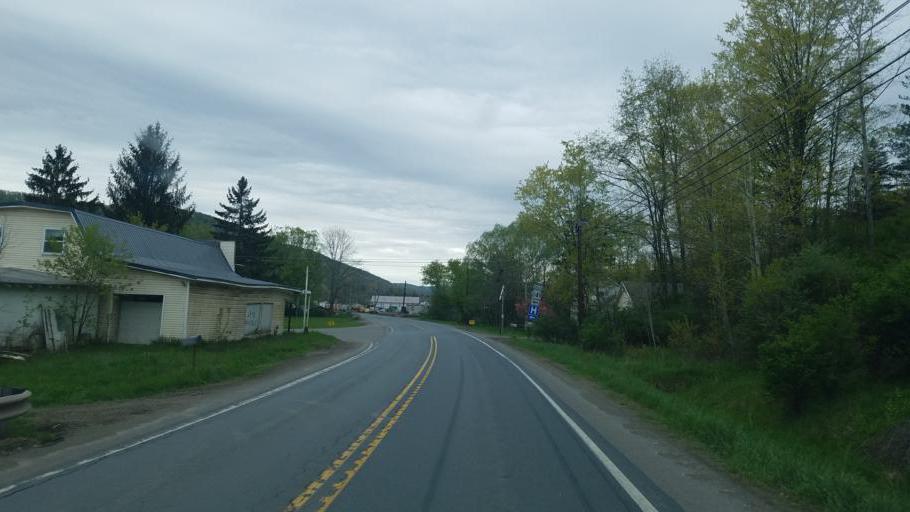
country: US
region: Pennsylvania
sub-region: Tioga County
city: Westfield
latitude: 41.9396
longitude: -77.4827
